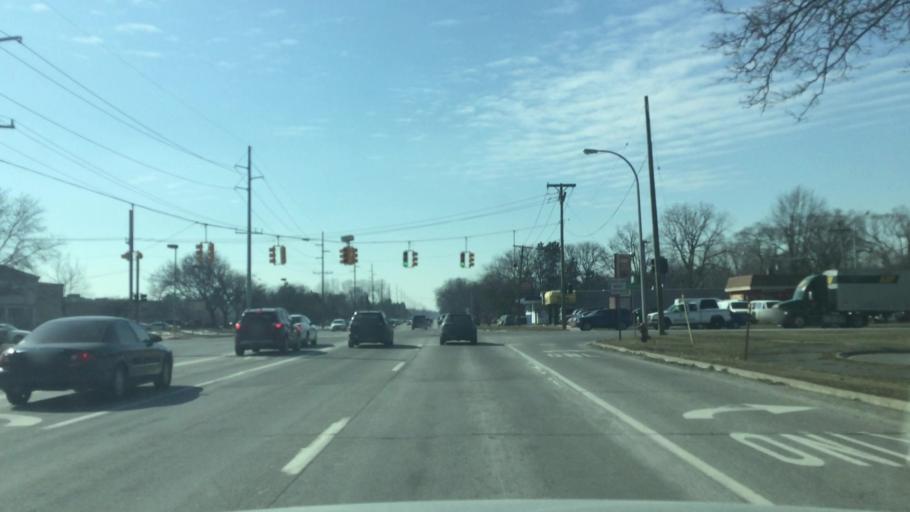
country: US
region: Michigan
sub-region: Wayne County
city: Garden City
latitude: 42.3109
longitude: -83.3491
